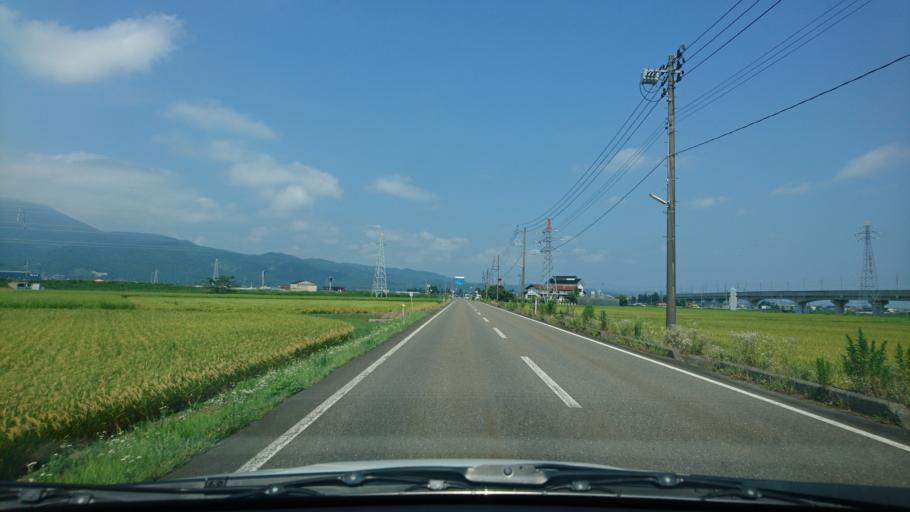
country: JP
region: Niigata
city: Arai
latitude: 37.0637
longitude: 138.2659
